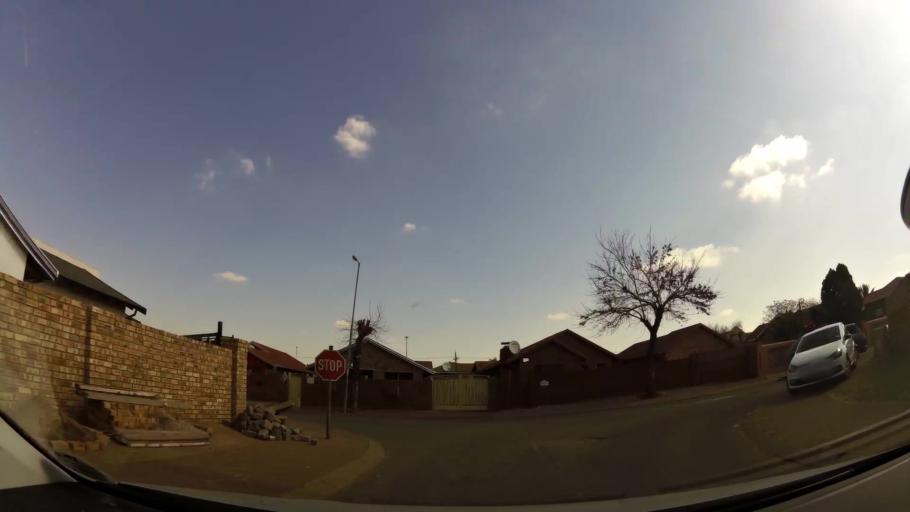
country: ZA
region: Gauteng
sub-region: City of Johannesburg Metropolitan Municipality
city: Soweto
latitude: -26.2647
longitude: 27.8850
